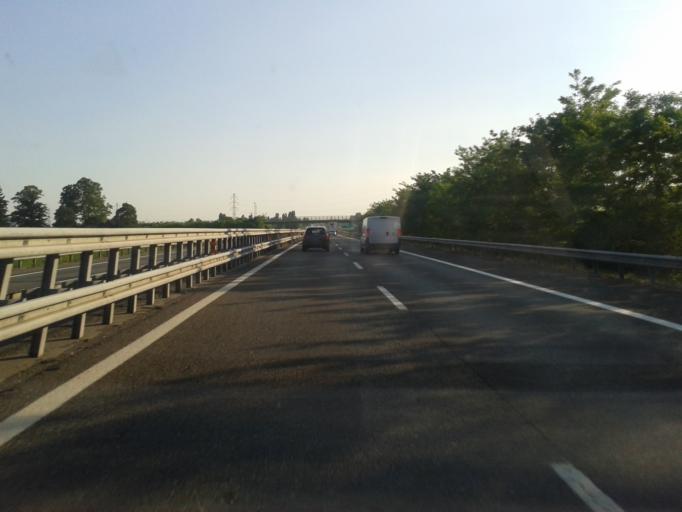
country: IT
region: Piedmont
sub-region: Provincia di Alessandria
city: Castelnuovo Scrivia
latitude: 44.9414
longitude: 8.8928
